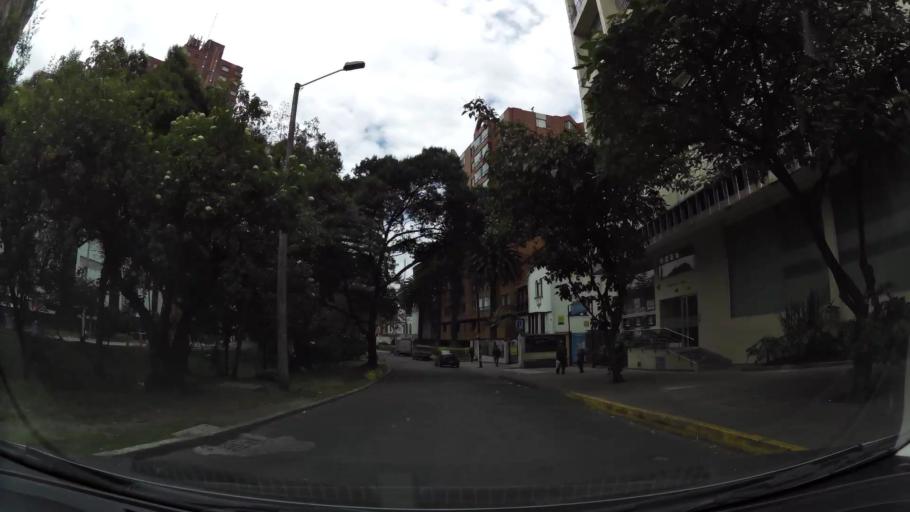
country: CO
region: Bogota D.C.
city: Bogota
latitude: 4.6265
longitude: -74.0662
